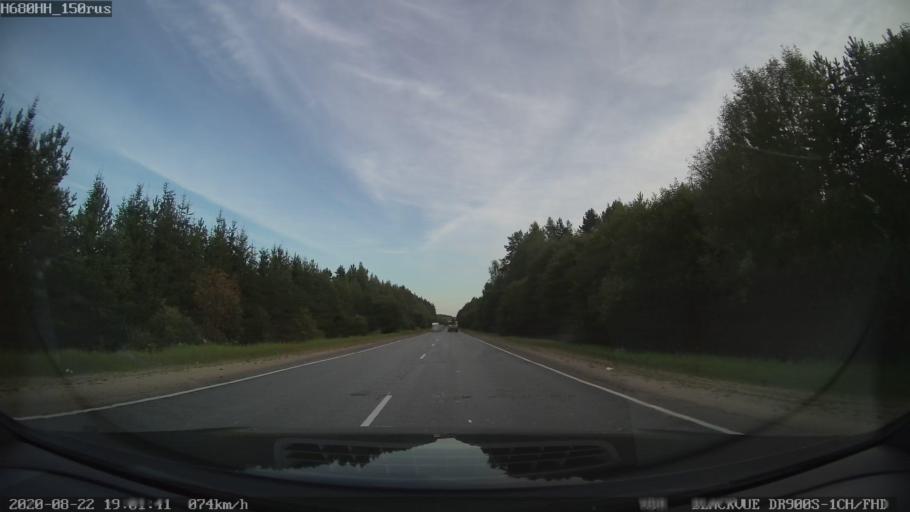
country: RU
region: Tverskaya
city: Vasil'yevskiy Mokh
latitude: 57.1167
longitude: 36.1162
